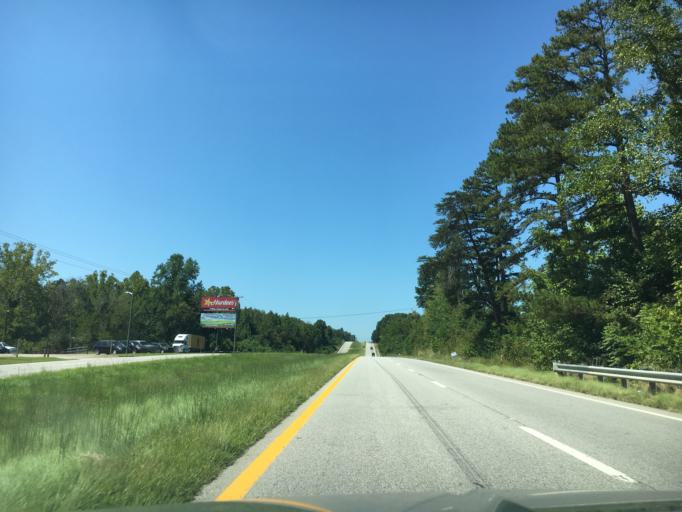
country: US
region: Virginia
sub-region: City of Danville
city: Danville
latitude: 36.5809
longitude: -79.2898
